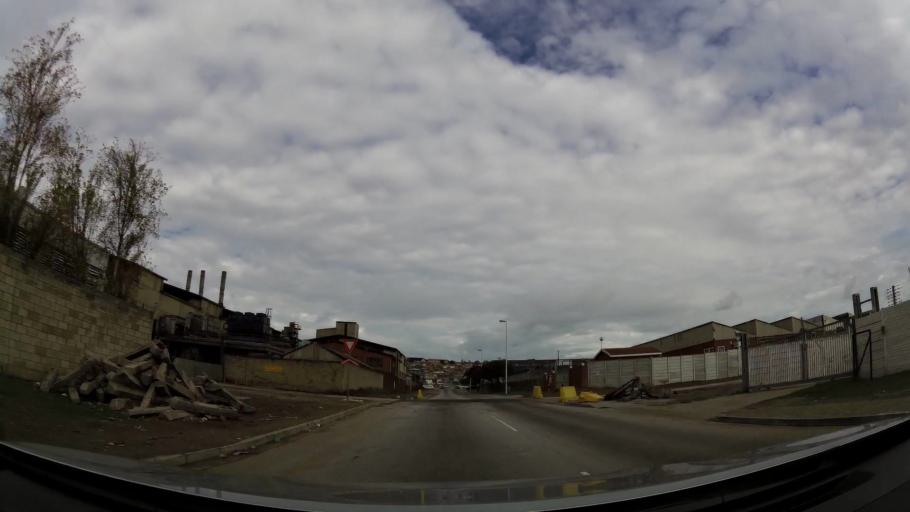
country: ZA
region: Eastern Cape
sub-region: Nelson Mandela Bay Metropolitan Municipality
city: Port Elizabeth
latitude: -33.9288
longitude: 25.5791
